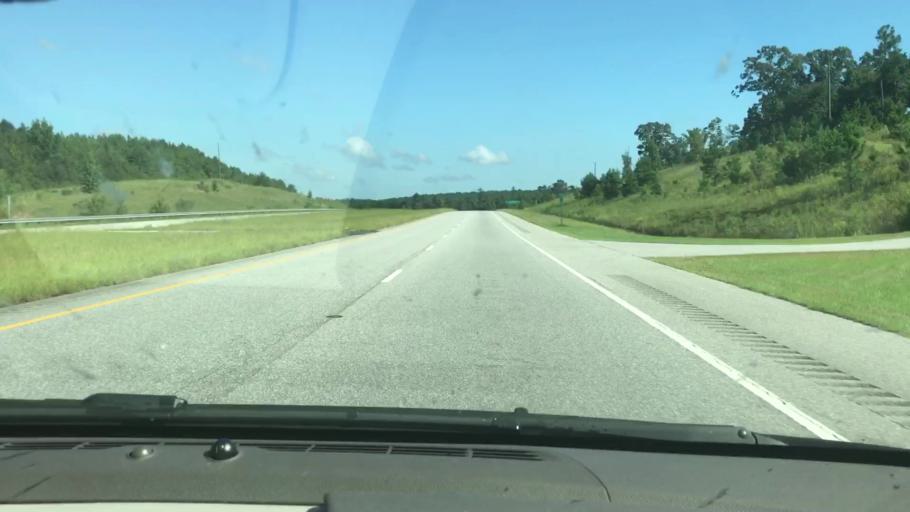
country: US
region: Alabama
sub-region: Barbour County
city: Eufaula
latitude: 32.1107
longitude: -85.1498
